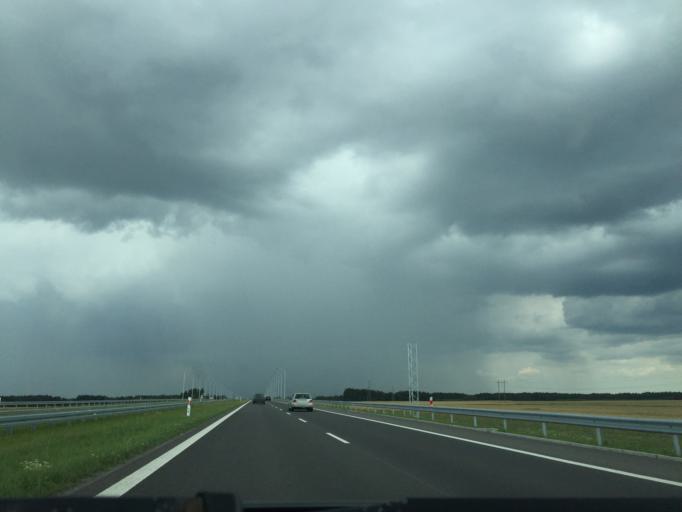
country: PL
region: Masovian Voivodeship
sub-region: Powiat szydlowiecki
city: Oronsko
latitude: 51.2912
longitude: 20.9829
